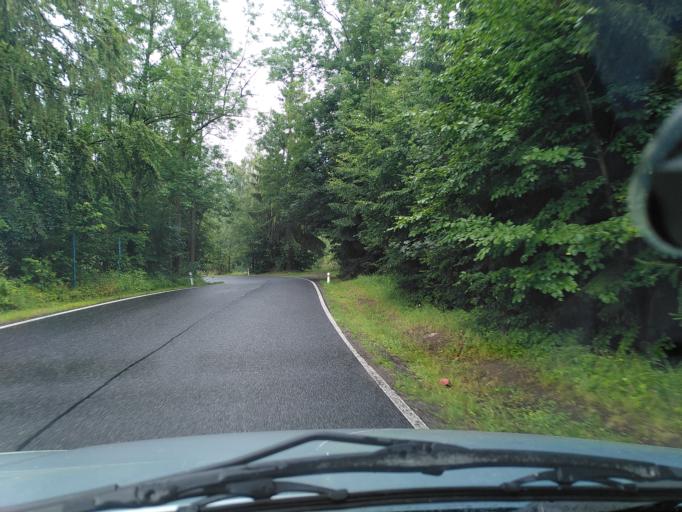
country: CZ
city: Novy Bor
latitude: 50.7935
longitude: 14.5400
